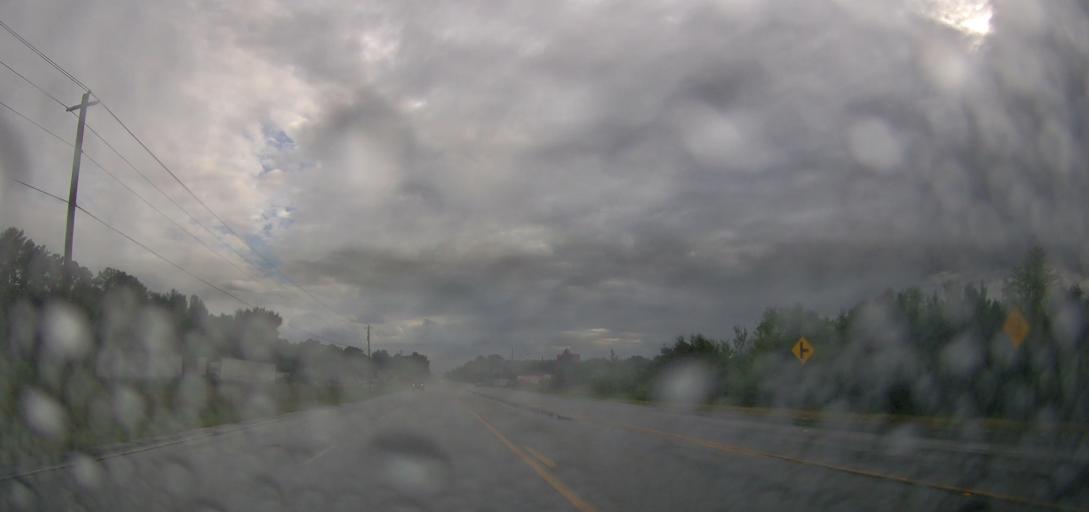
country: US
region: Georgia
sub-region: Ware County
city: Sunnyside
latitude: 31.2430
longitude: -82.3174
